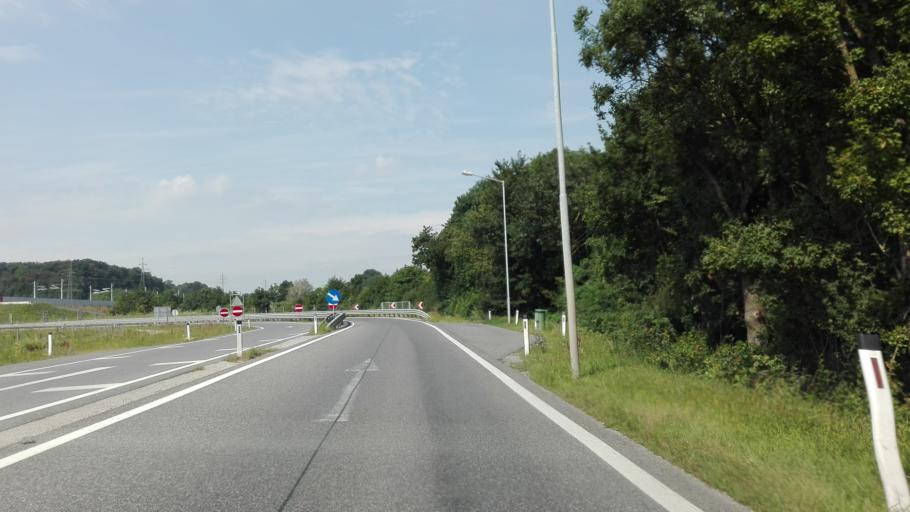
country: AT
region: Lower Austria
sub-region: Sankt Polten Stadt
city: Sankt Poelten
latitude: 48.1785
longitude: 15.6147
